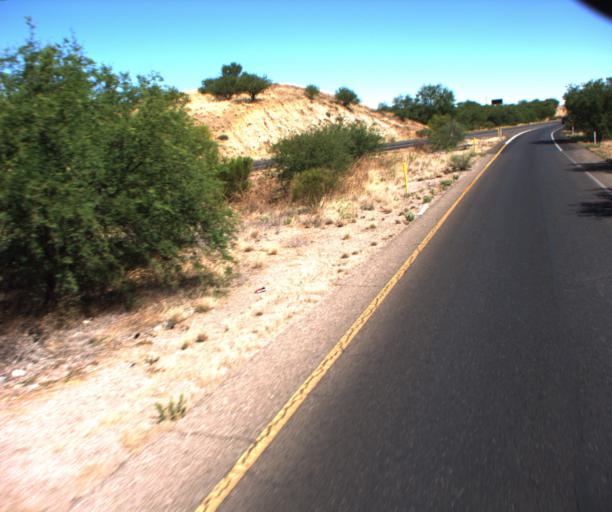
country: US
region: Arizona
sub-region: Santa Cruz County
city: Nogales
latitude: 31.3999
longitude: -110.9601
